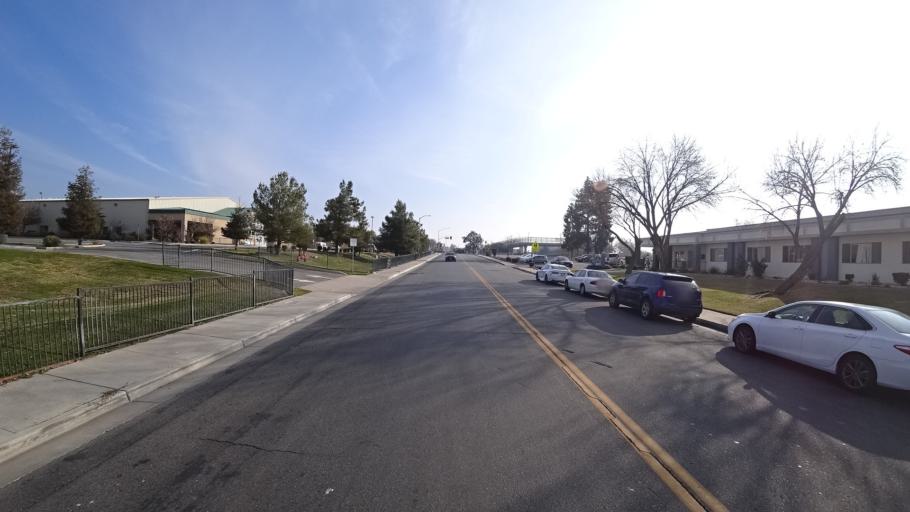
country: US
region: California
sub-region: Kern County
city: Bakersfield
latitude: 35.3939
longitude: -118.9735
